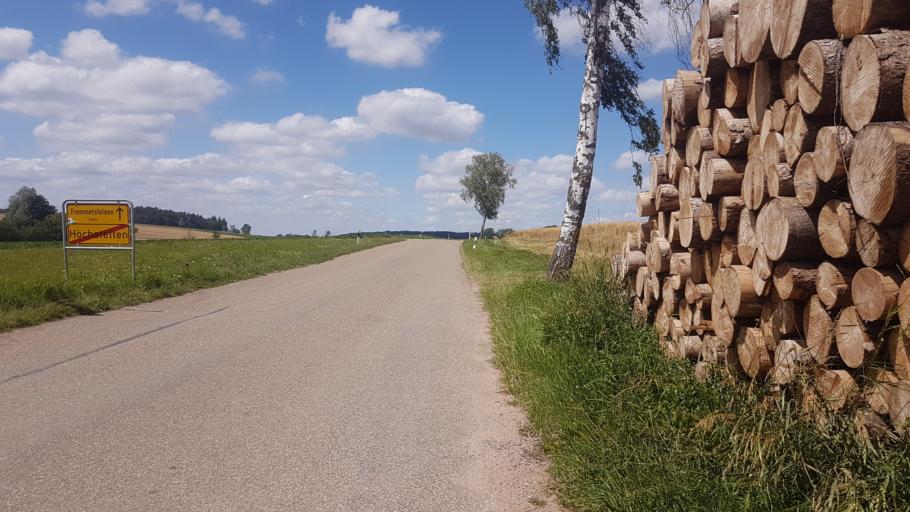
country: DE
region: Bavaria
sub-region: Regierungsbezirk Mittelfranken
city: Colmberg
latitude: 49.3289
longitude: 10.3773
